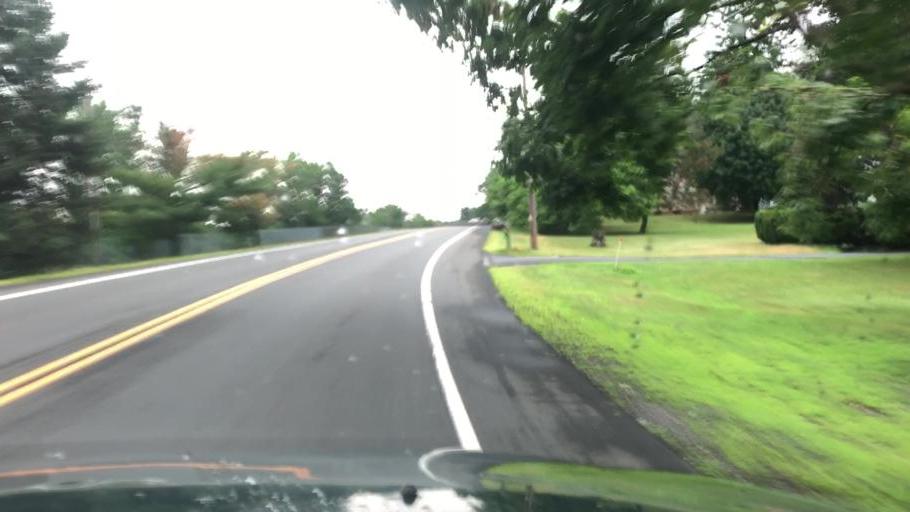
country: US
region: New York
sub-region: Dutchess County
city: Beacon
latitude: 41.5274
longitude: -73.9421
